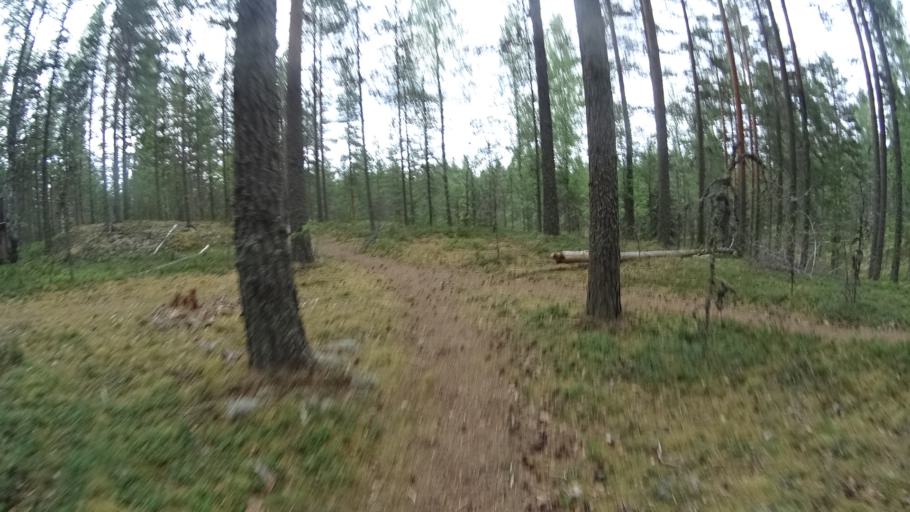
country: FI
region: Satakunta
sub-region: Pohjois-Satakunta
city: Jaemijaervi
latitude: 61.7736
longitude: 22.7317
